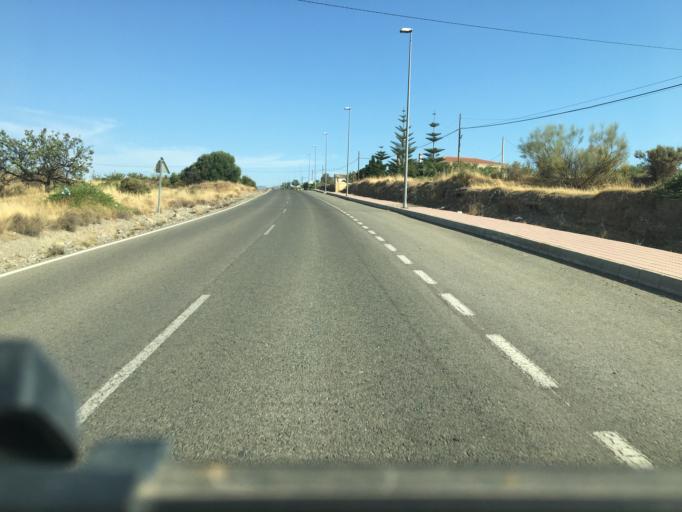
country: ES
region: Andalusia
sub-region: Provincia de Almeria
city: Huercal-Overa
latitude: 37.4452
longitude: -1.9818
